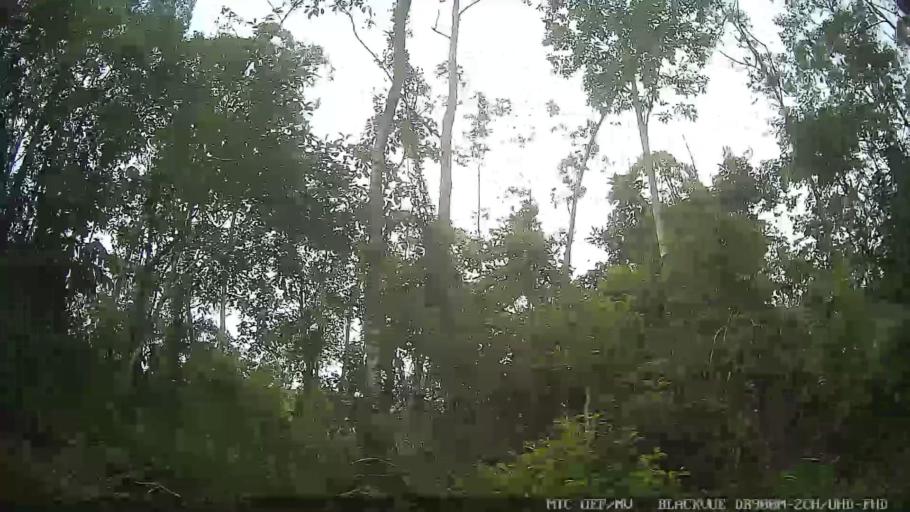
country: BR
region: Sao Paulo
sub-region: Aruja
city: Aruja
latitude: -23.4011
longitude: -46.2355
